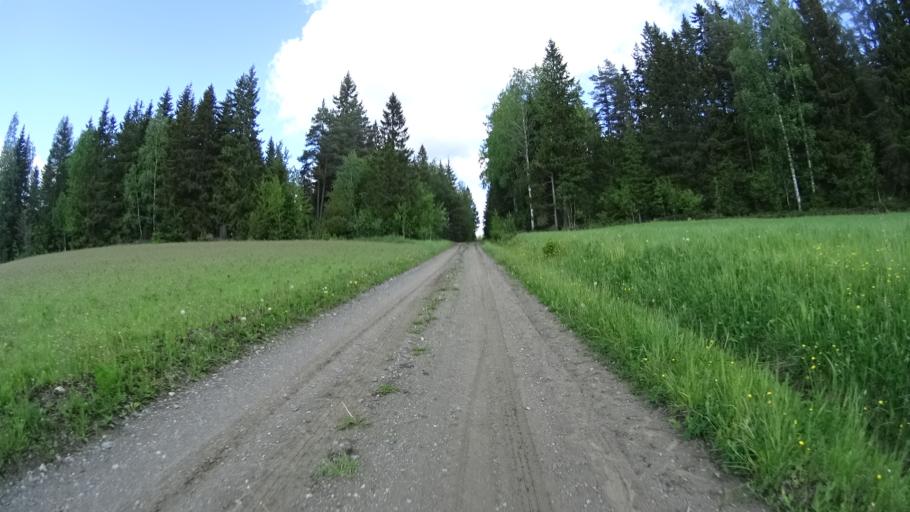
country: FI
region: Uusimaa
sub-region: Raaseporin
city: Karis
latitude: 60.1484
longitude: 23.6229
